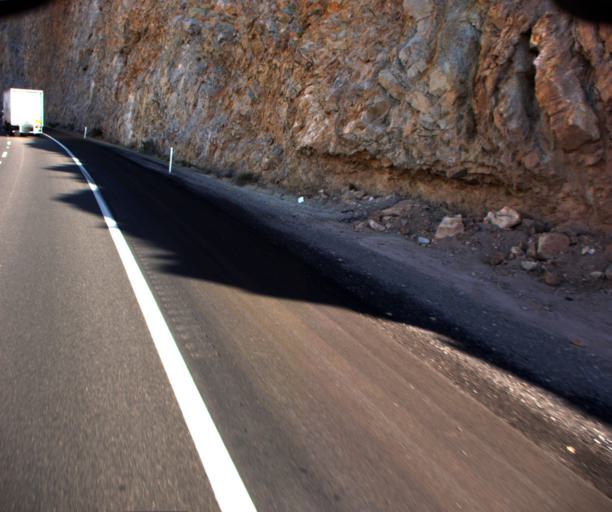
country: US
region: Arizona
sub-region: Mohave County
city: Beaver Dam
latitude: 36.9180
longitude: -113.8645
